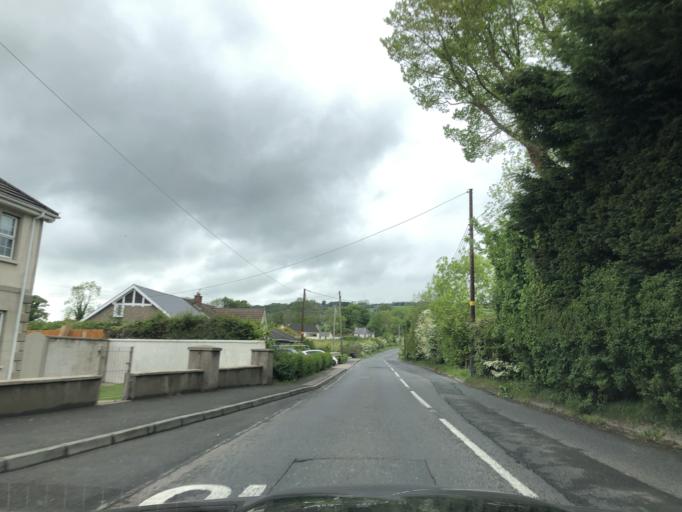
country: GB
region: Northern Ireland
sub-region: Lisburn District
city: Lisburn
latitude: 54.5319
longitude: -6.0708
